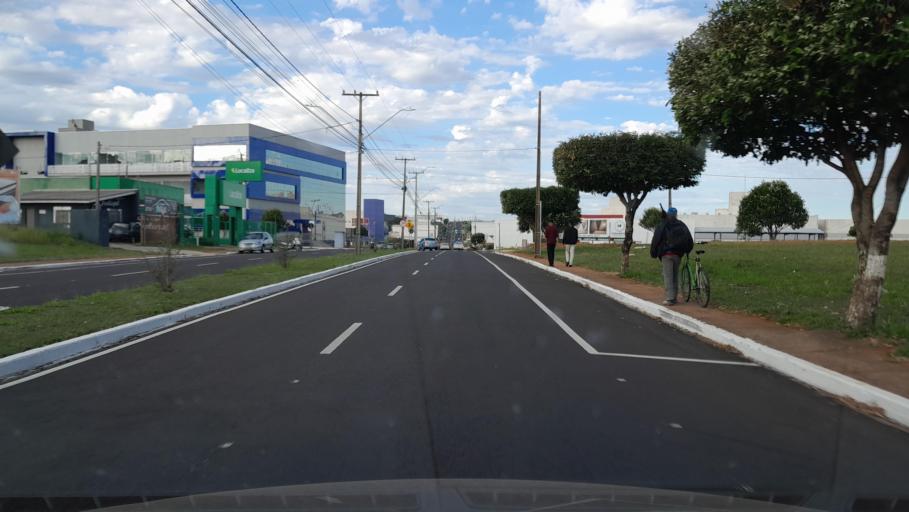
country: BR
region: Parana
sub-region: Umuarama
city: Umuarama
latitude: -23.7550
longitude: -53.2825
